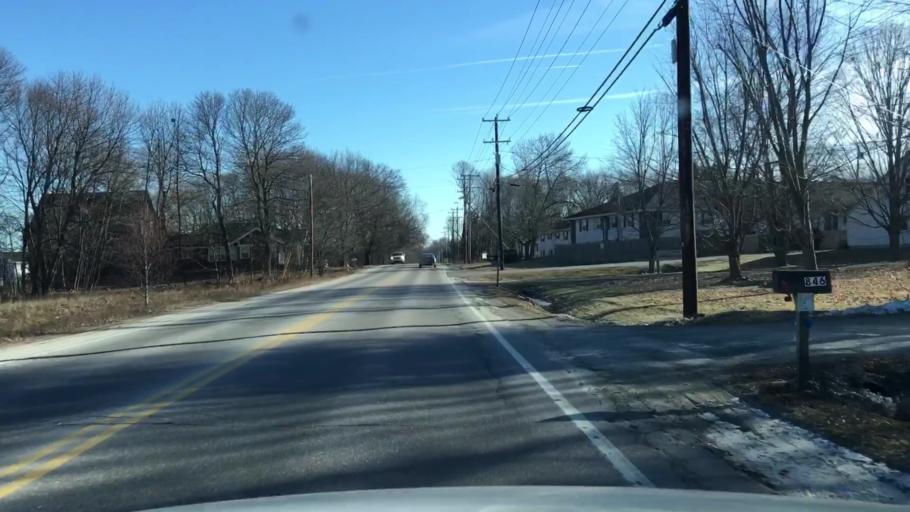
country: US
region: Maine
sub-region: Penobscot County
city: Bangor
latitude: 44.8198
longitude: -68.8033
